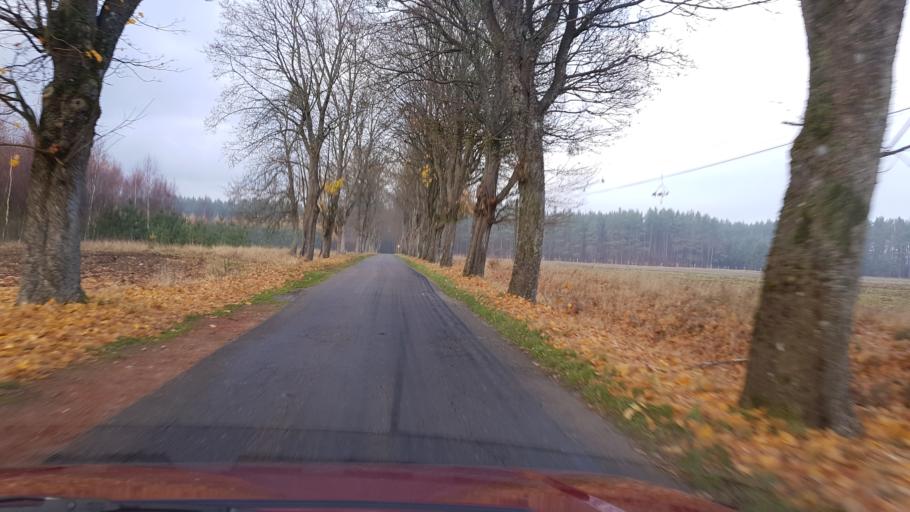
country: PL
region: West Pomeranian Voivodeship
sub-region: Powiat bialogardzki
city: Tychowo
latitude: 53.9646
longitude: 16.3167
